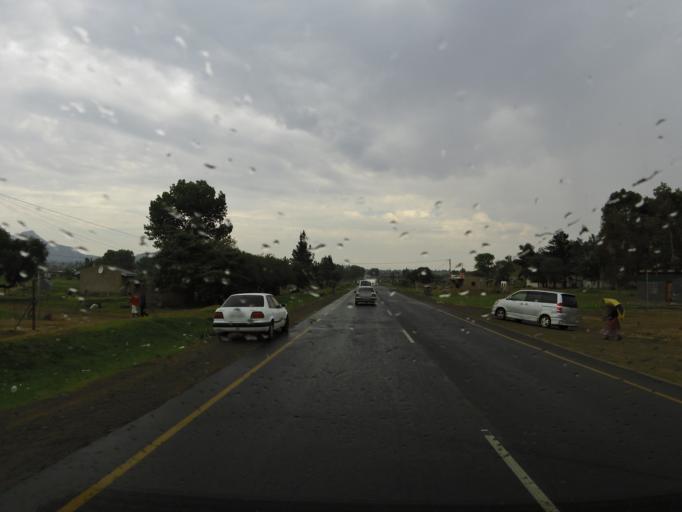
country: LS
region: Mafeteng
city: Mafeteng
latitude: -29.7945
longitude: 27.2617
